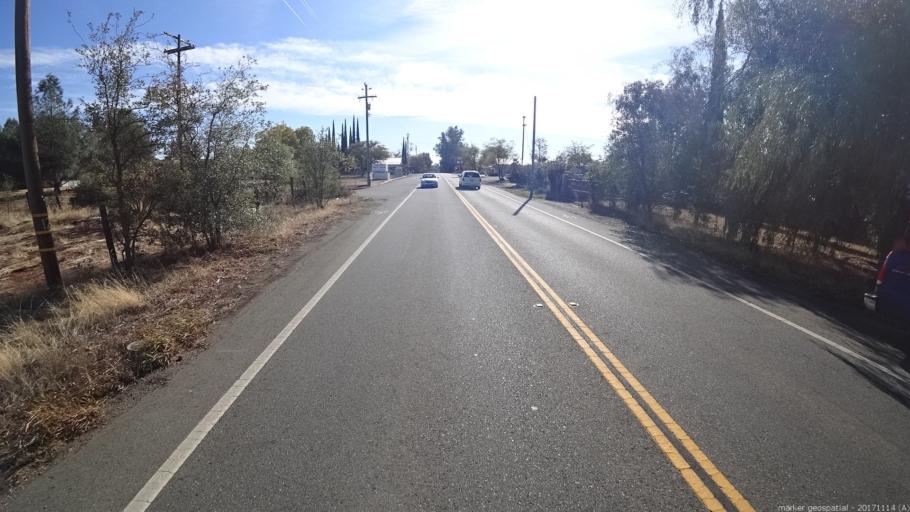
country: US
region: California
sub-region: Shasta County
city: Anderson
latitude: 40.4449
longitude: -122.4078
